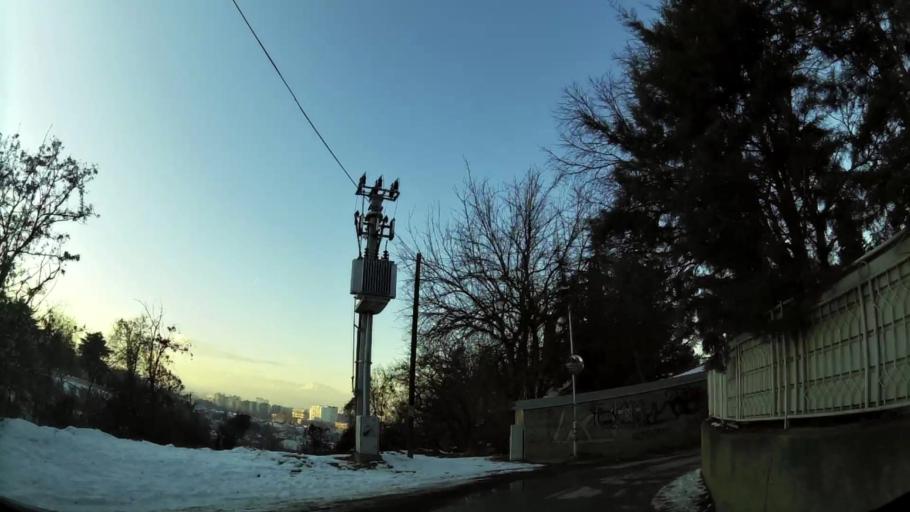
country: MK
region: Karpos
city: Skopje
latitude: 41.9906
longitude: 21.4072
